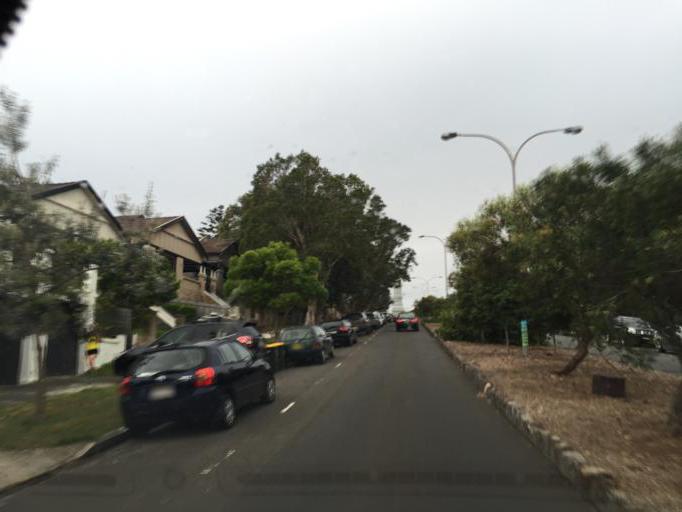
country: AU
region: New South Wales
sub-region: Waverley
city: North Bondi
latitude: -33.8858
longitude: 151.2822
